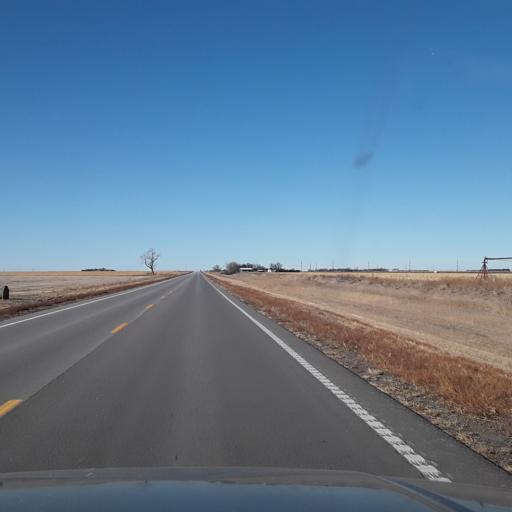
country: US
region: Nebraska
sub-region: Gosper County
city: Elwood
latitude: 40.5337
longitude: -99.6475
